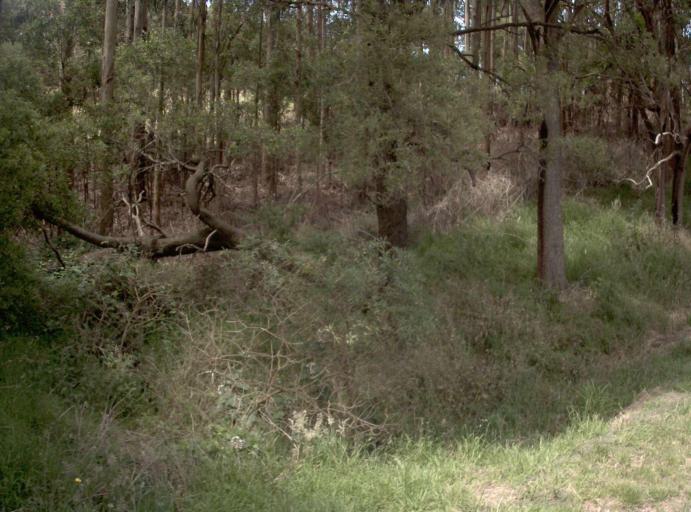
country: AU
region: Victoria
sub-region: Bass Coast
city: North Wonthaggi
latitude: -38.7271
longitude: 146.1214
